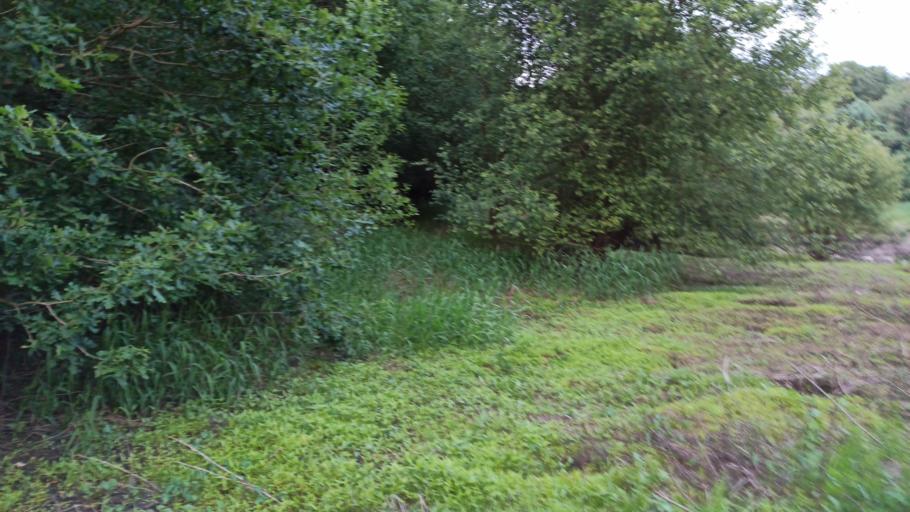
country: ES
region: Galicia
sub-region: Provincia da Coruna
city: Negreira
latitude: 42.9010
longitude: -8.7378
